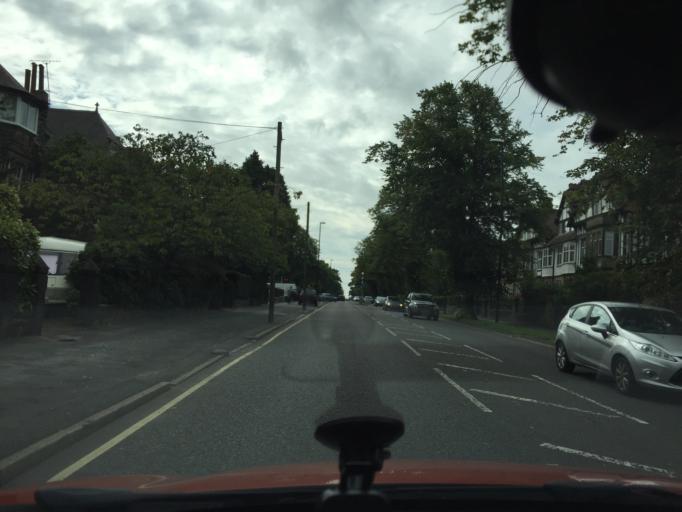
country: GB
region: England
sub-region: North Yorkshire
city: Harrogate
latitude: 53.9816
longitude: -1.5360
